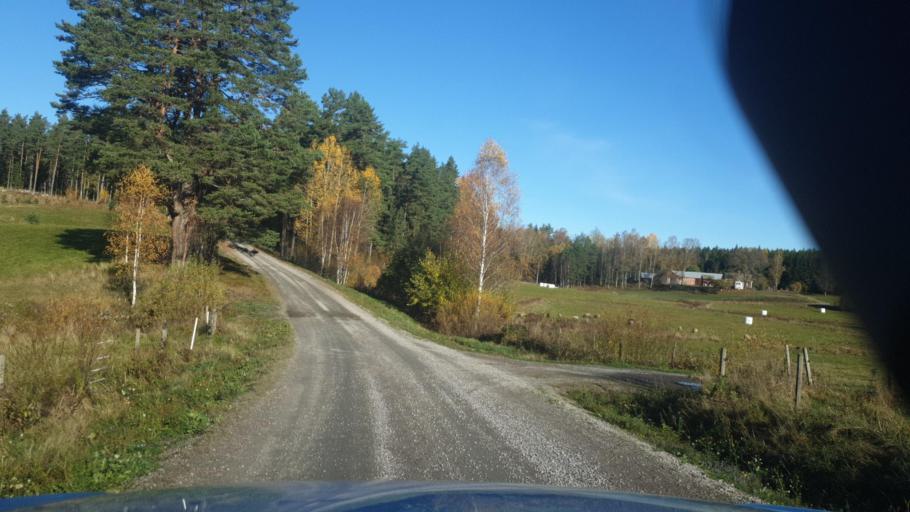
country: SE
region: Vaermland
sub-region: Arvika Kommun
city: Arvika
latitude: 59.5661
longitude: 12.7414
